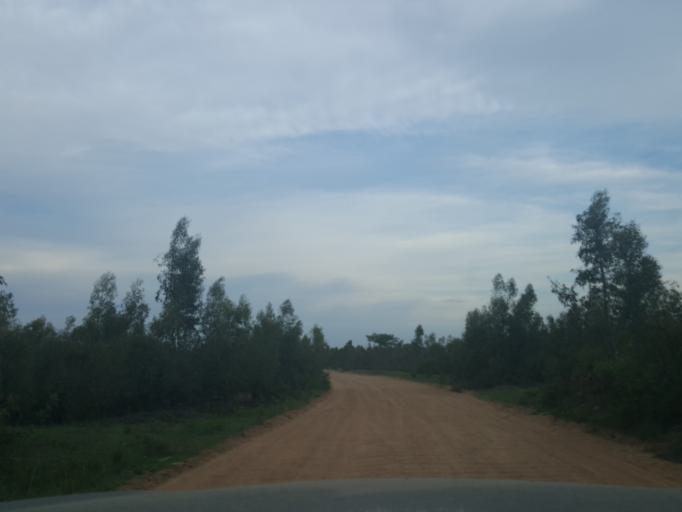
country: ZA
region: Limpopo
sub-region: Mopani District Municipality
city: Hoedspruit
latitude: -24.5879
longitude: 30.9637
